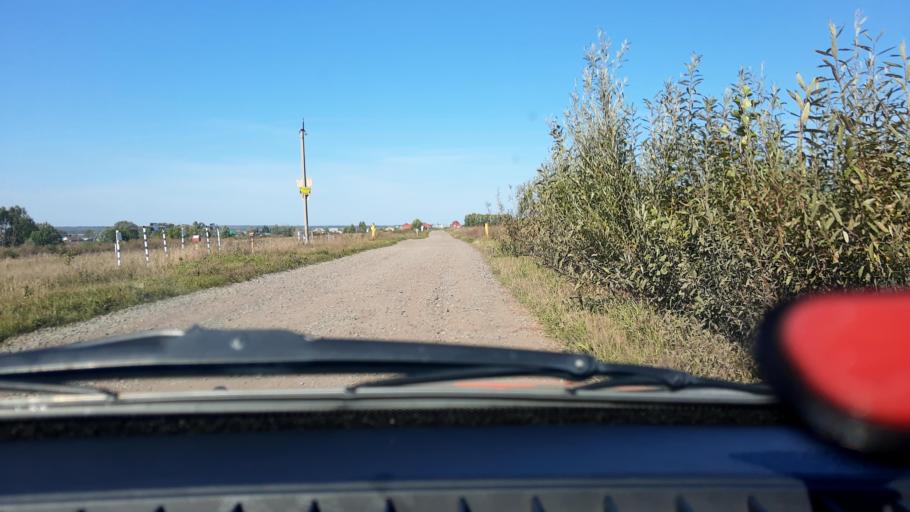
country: RU
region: Bashkortostan
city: Asanovo
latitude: 54.8062
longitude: 55.5858
